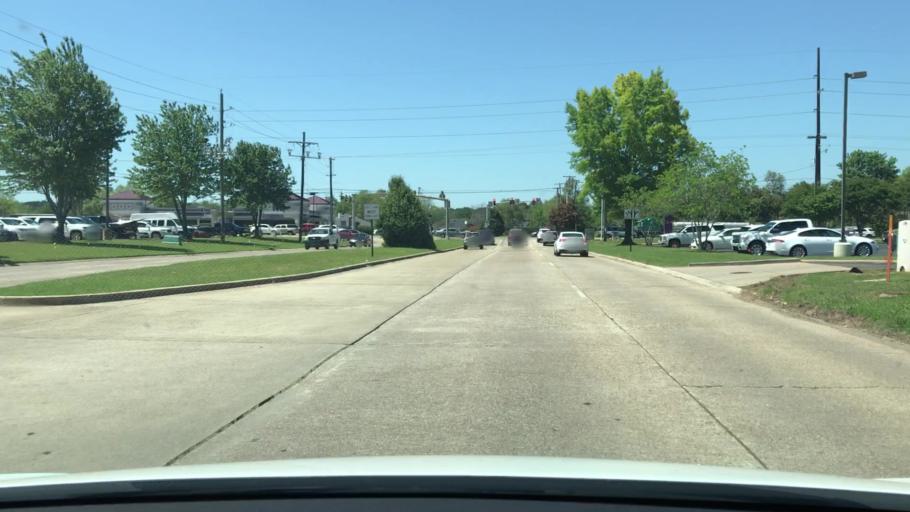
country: US
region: Louisiana
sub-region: Bossier Parish
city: Bossier City
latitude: 32.4269
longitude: -93.7166
